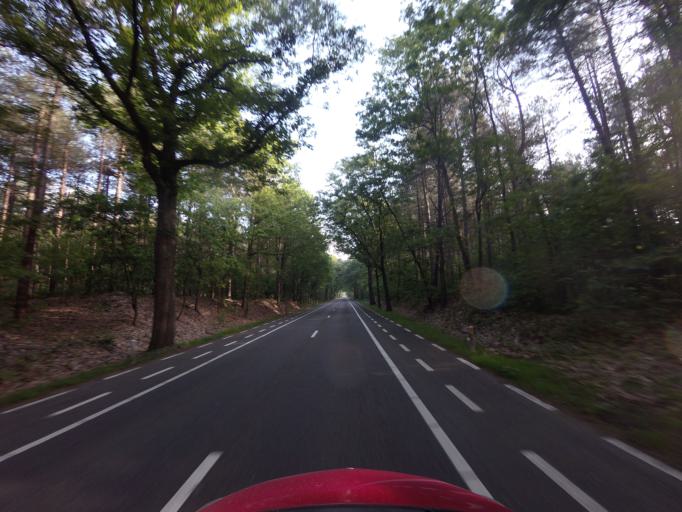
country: BE
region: Flanders
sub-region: Provincie Limburg
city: Overpelt
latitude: 51.2058
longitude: 5.3629
